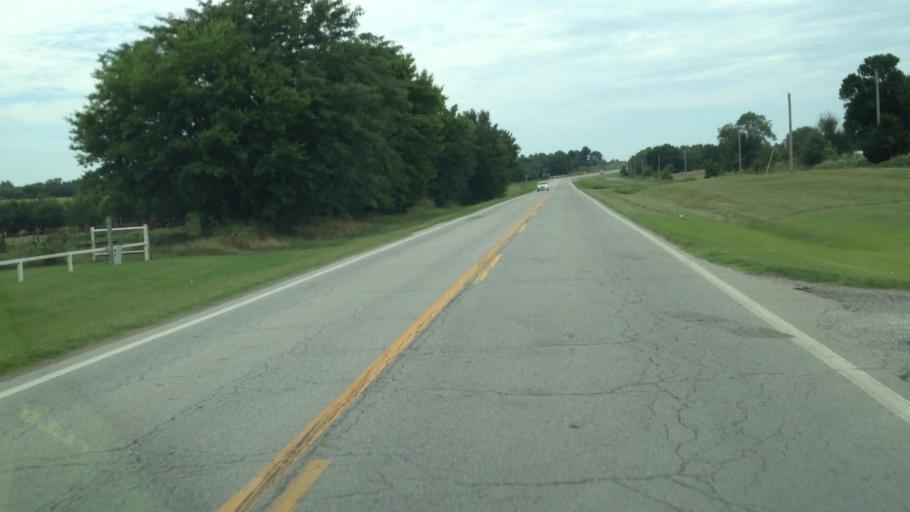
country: US
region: Kansas
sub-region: Labette County
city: Chetopa
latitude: 36.8808
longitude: -95.0989
